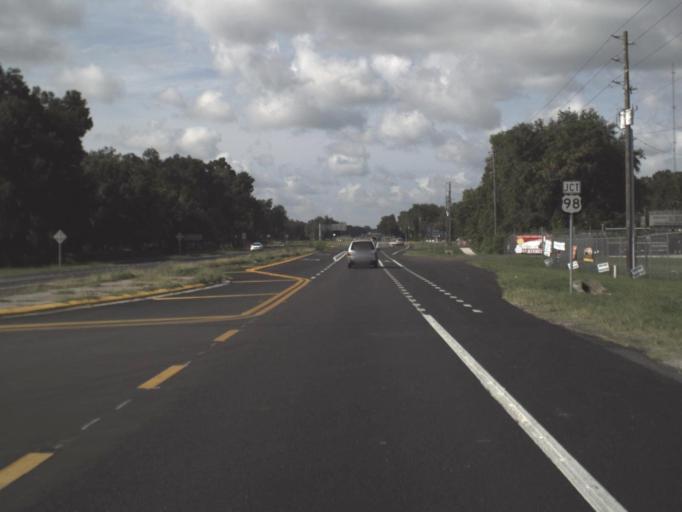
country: US
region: Florida
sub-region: Pasco County
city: Lacoochee
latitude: 28.4577
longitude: -82.1853
